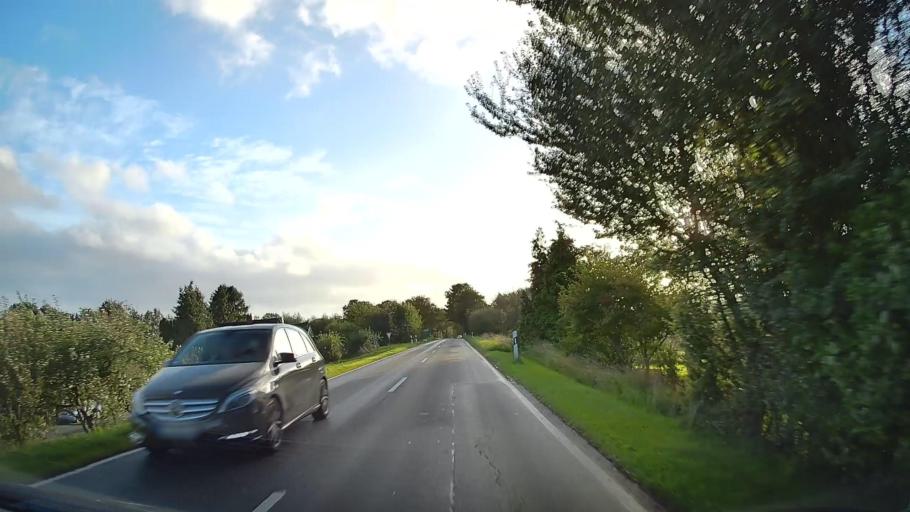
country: DE
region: Schleswig-Holstein
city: Herzhorn
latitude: 53.7902
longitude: 9.4855
